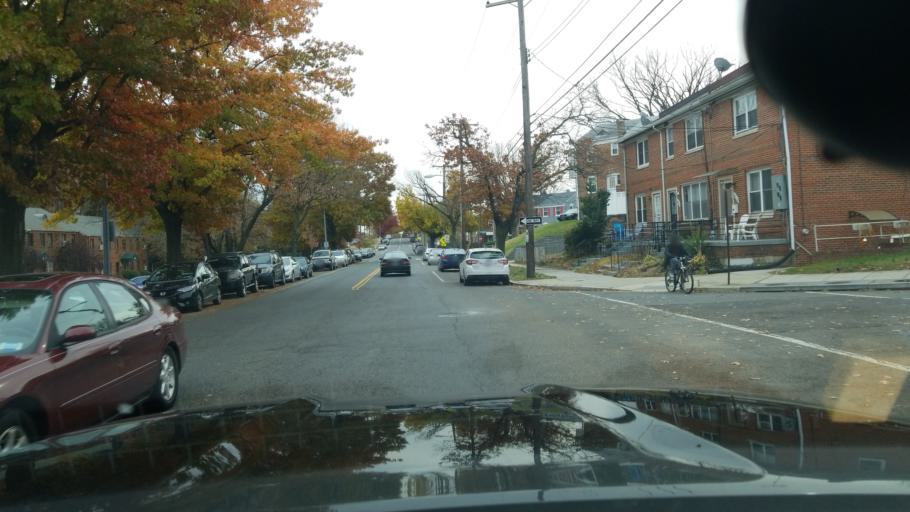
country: US
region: Maryland
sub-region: Prince George's County
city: Chillum
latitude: 38.9645
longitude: -77.0009
